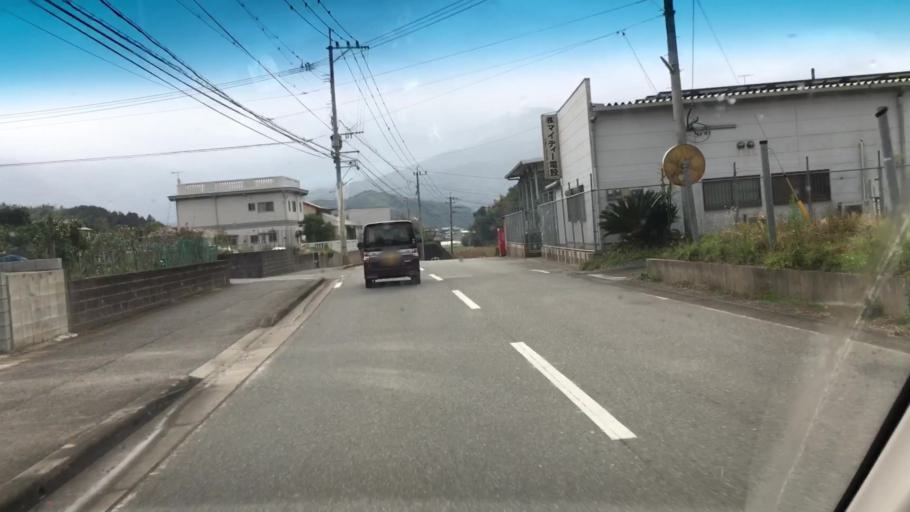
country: JP
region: Fukuoka
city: Maebaru-chuo
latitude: 33.5285
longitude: 130.1965
